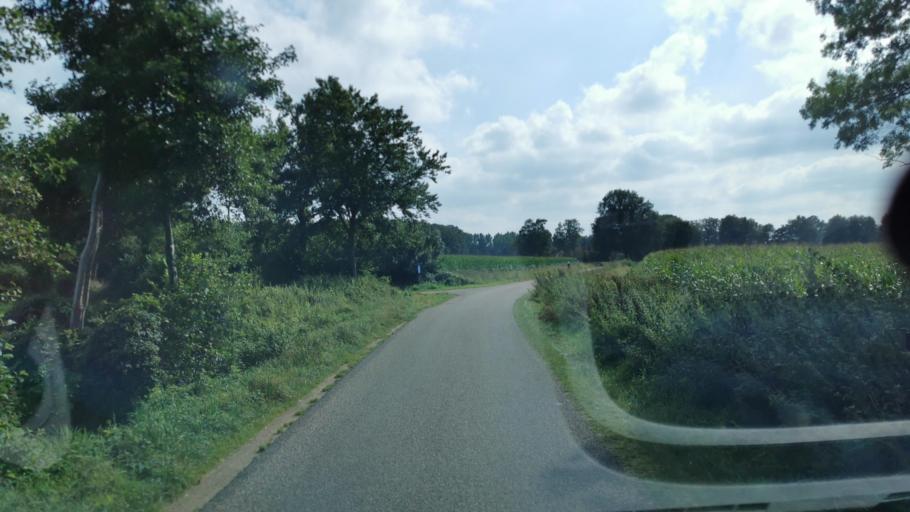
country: NL
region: Overijssel
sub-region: Gemeente Hengelo
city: Hengelo
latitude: 52.3324
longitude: 6.8442
